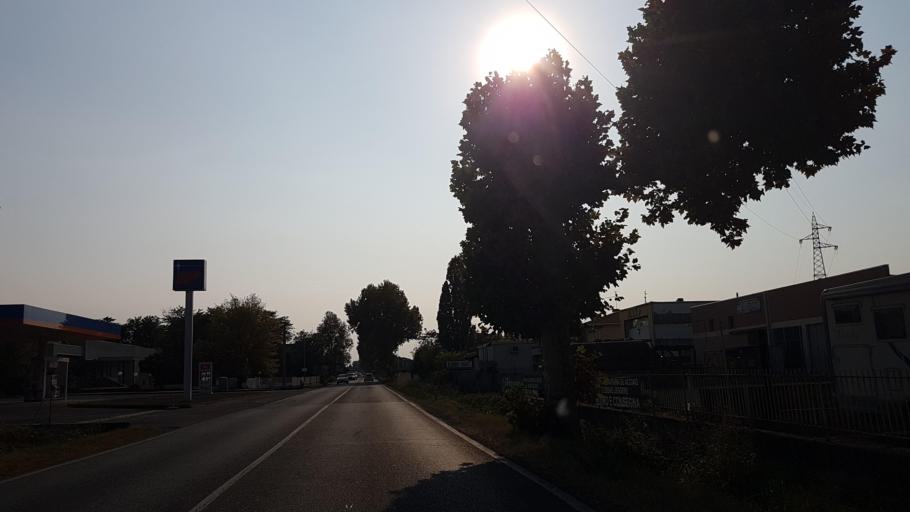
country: IT
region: Emilia-Romagna
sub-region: Provincia di Parma
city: Vicofertile
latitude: 44.7727
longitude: 10.2676
